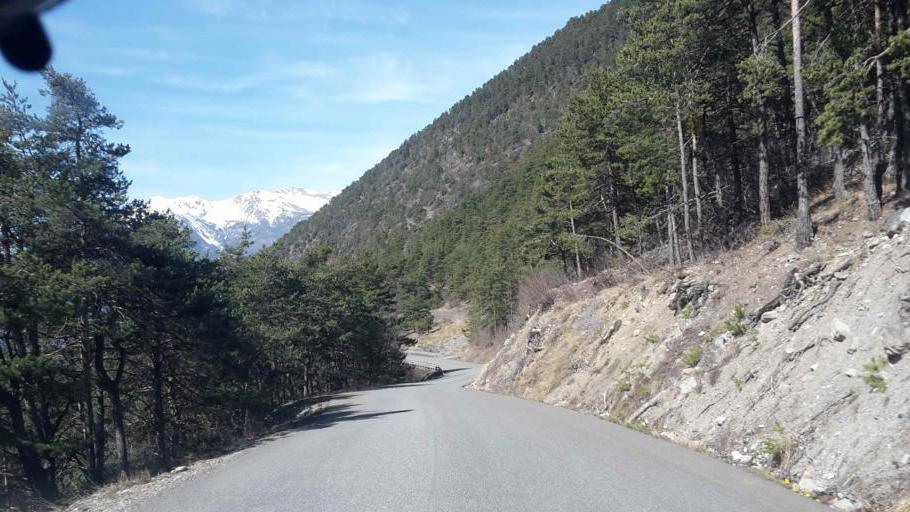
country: FR
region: Provence-Alpes-Cote d'Azur
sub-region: Departement des Hautes-Alpes
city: Embrun
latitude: 44.5558
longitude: 6.5722
